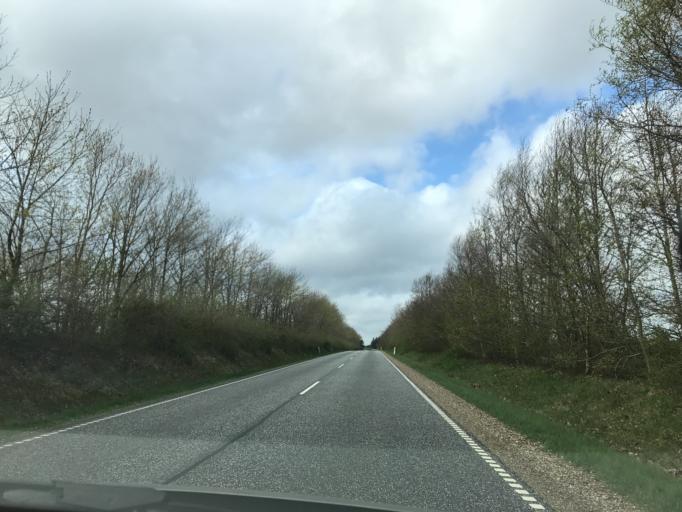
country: DK
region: Central Jutland
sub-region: Skive Kommune
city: Skive
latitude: 56.4164
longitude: 8.9783
